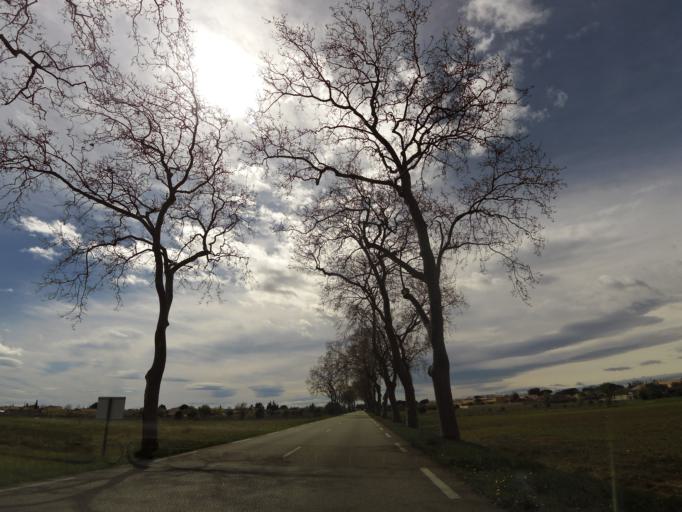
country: FR
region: Languedoc-Roussillon
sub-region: Departement du Gard
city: Codognan
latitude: 43.7318
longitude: 4.2299
